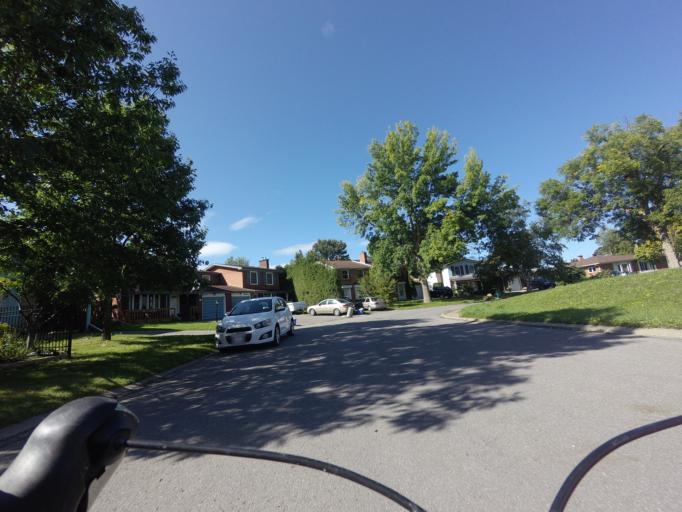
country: CA
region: Ontario
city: Bells Corners
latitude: 45.3182
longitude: -75.8365
